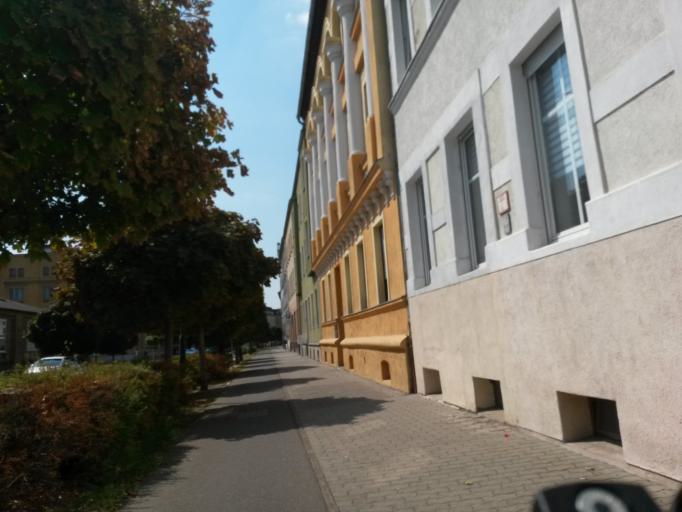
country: DE
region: Saxony-Anhalt
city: Wittenburg
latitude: 51.8692
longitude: 12.6569
